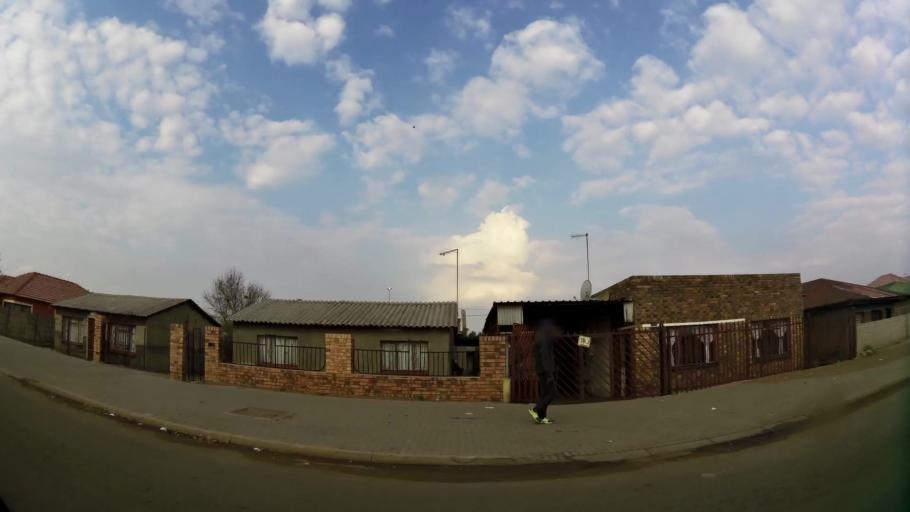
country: ZA
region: Gauteng
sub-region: Sedibeng District Municipality
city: Vanderbijlpark
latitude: -26.6949
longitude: 27.8658
